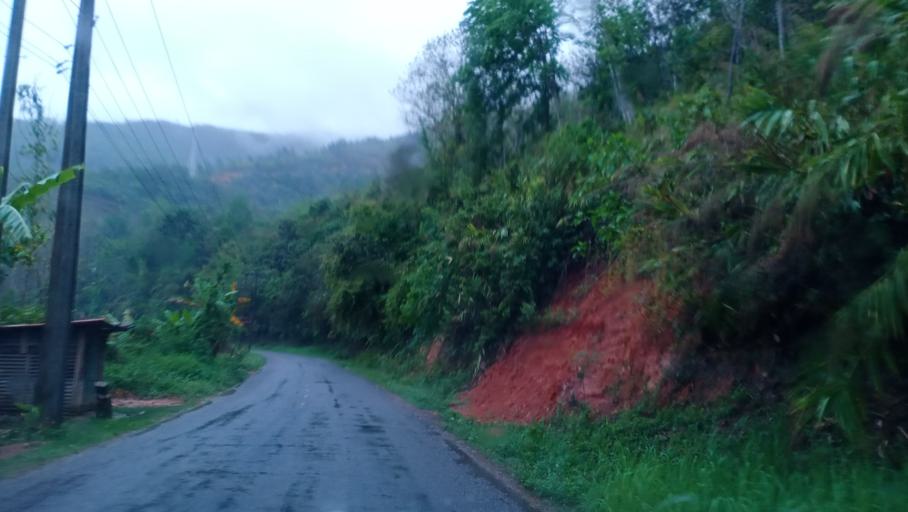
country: LA
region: Phongsali
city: Khoa
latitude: 21.0644
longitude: 102.4791
